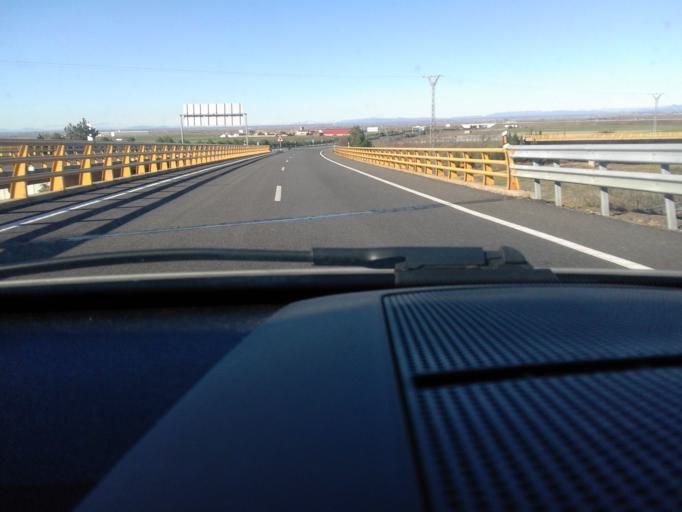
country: ES
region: Castille and Leon
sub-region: Provincia de Leon
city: Santas Martas
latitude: 42.4452
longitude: -5.3811
